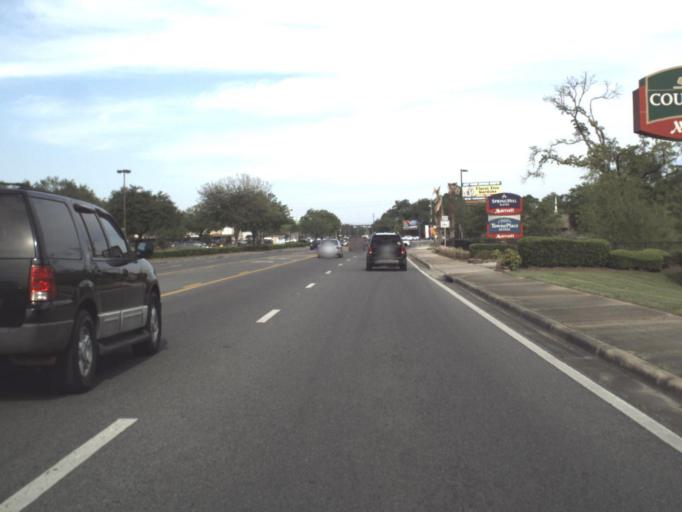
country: US
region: Florida
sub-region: Escambia County
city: Ferry Pass
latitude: 30.4960
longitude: -87.2258
